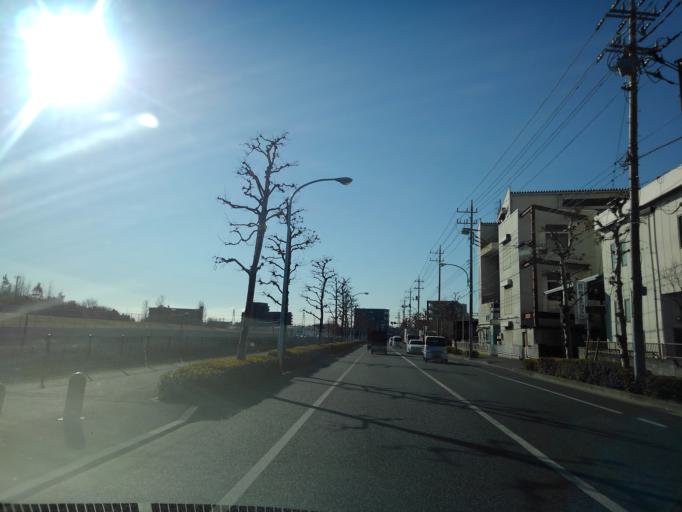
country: JP
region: Tokyo
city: Fussa
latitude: 35.7334
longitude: 139.3830
